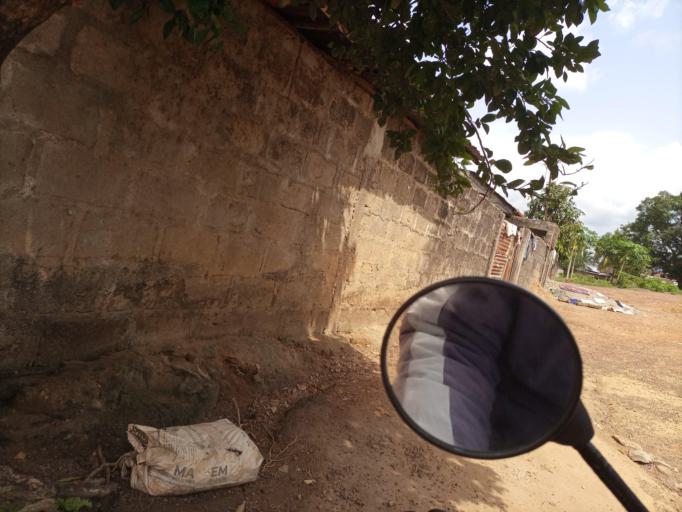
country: SL
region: Southern Province
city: Bo
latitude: 7.9467
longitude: -11.7348
